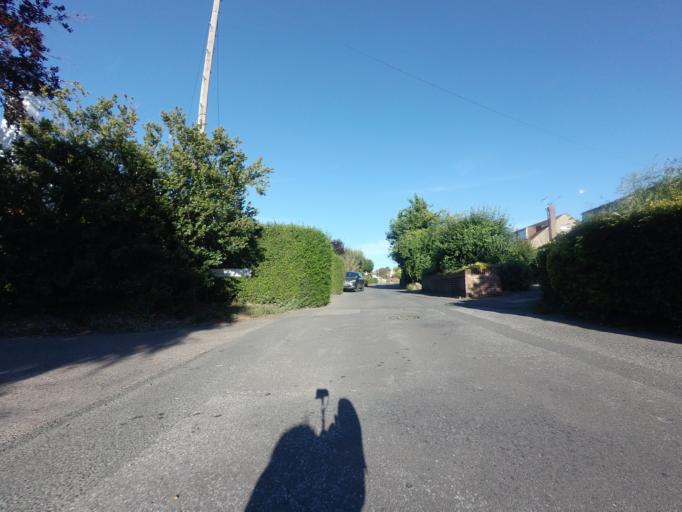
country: GB
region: England
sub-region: Kent
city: Herne Bay
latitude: 51.3619
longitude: 1.1269
